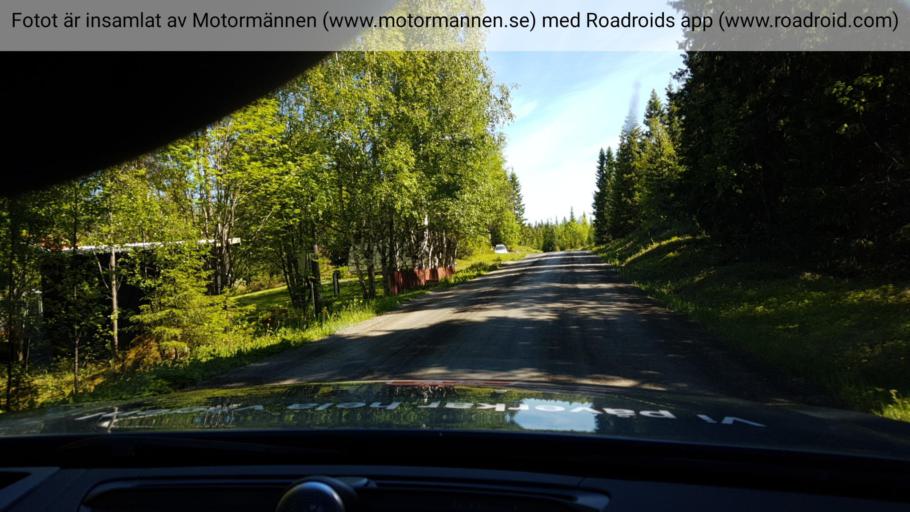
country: SE
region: Jaemtland
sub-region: OEstersunds Kommun
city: Brunflo
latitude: 63.0084
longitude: 14.7876
